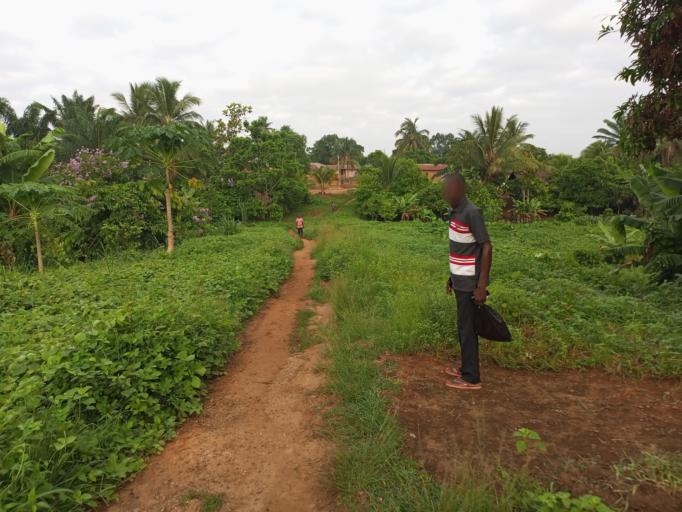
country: SL
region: Eastern Province
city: Pendembu
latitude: 8.0999
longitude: -10.6974
